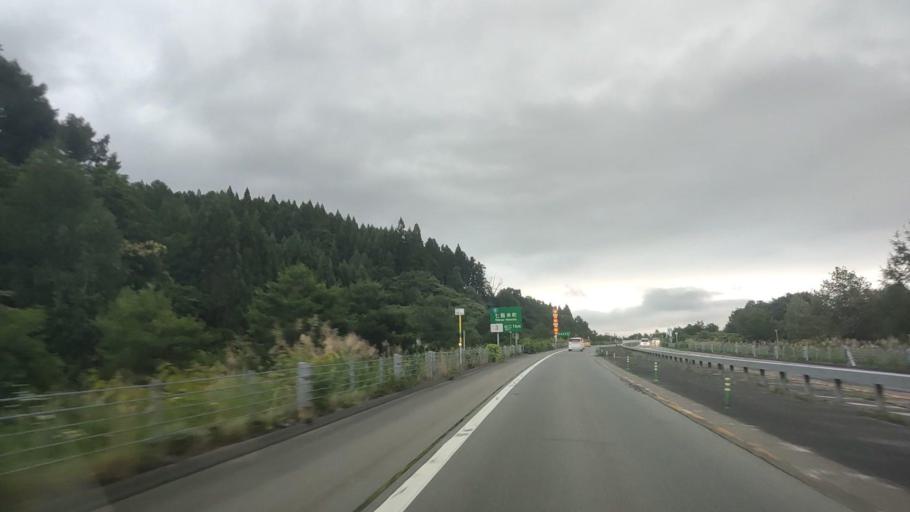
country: JP
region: Hokkaido
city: Nanae
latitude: 41.9083
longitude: 140.6957
